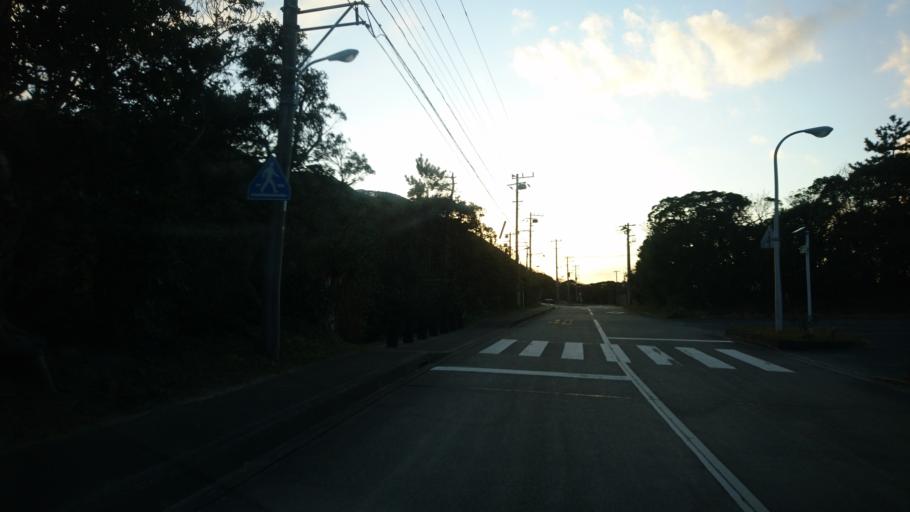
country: JP
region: Shizuoka
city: Shimoda
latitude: 34.3635
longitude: 139.2566
